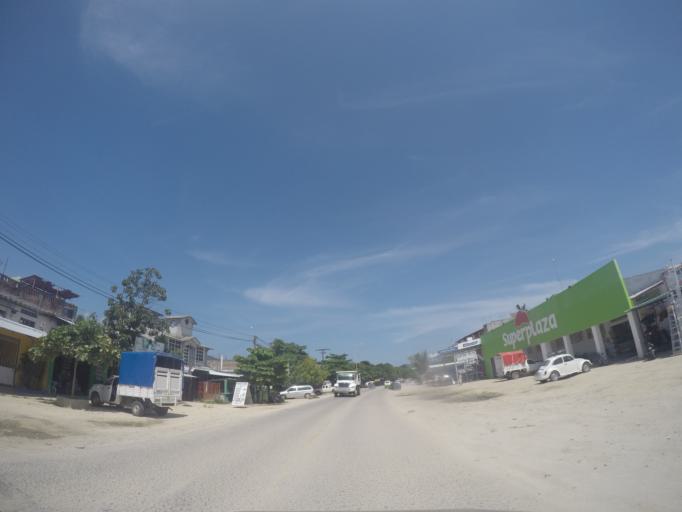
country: MX
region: Oaxaca
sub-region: Villa de Tututepec de Melchor Ocampo
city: Santa Rosa de Lima
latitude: 16.0107
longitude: -97.4367
